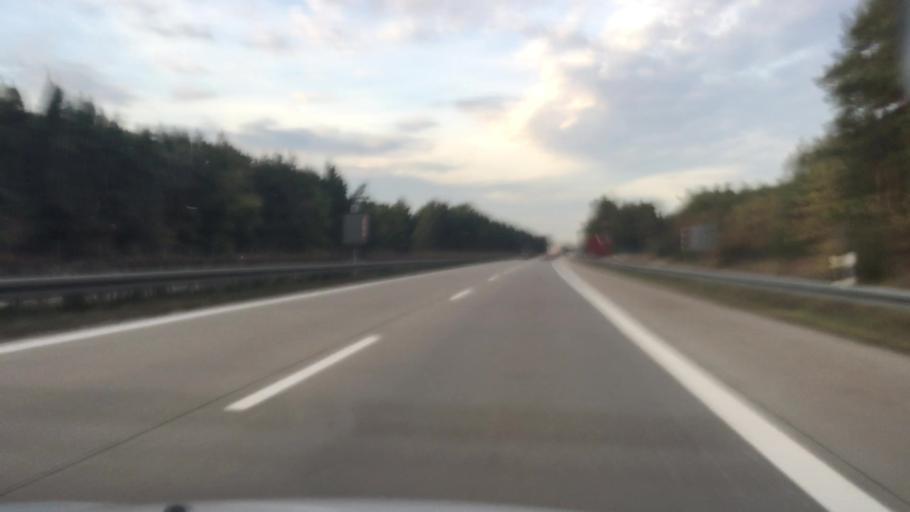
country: DE
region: Brandenburg
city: Ruhland
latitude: 51.4485
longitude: 13.8417
